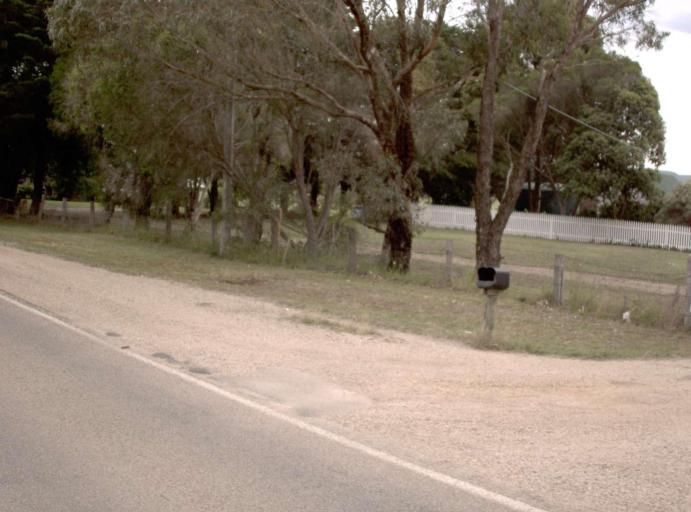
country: AU
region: Victoria
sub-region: East Gippsland
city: Bairnsdale
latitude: -37.8096
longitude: 147.4843
